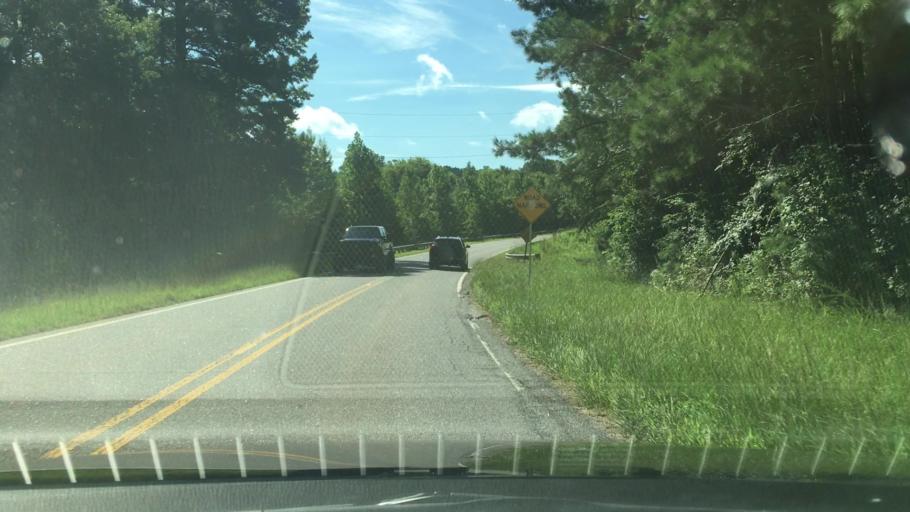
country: US
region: Georgia
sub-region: Putnam County
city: Jefferson
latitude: 33.3901
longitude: -83.2621
